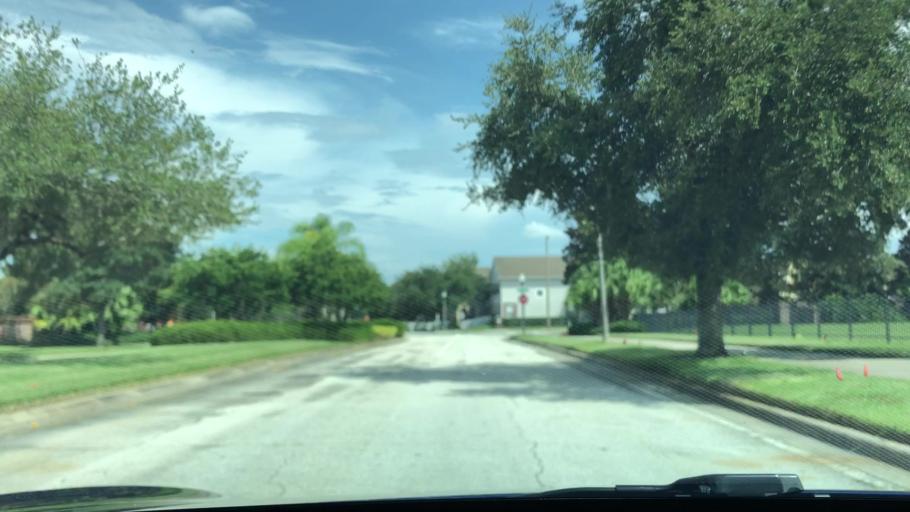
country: US
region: Florida
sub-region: Orange County
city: Conway
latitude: 28.4741
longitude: -81.2692
